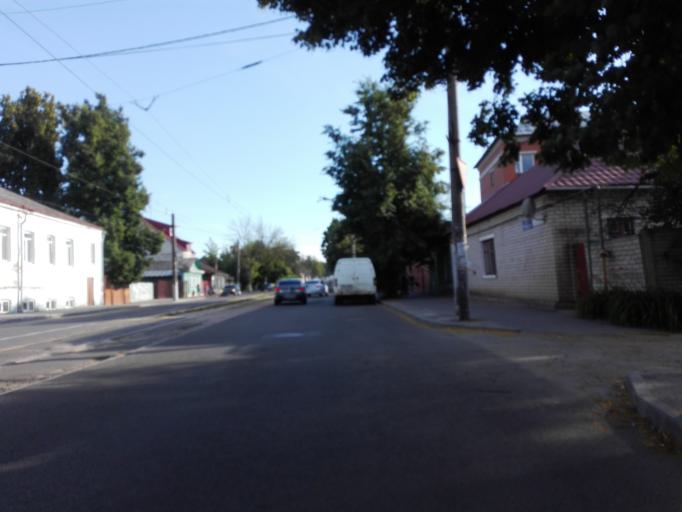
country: RU
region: Orjol
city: Orel
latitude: 52.9546
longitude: 36.0570
